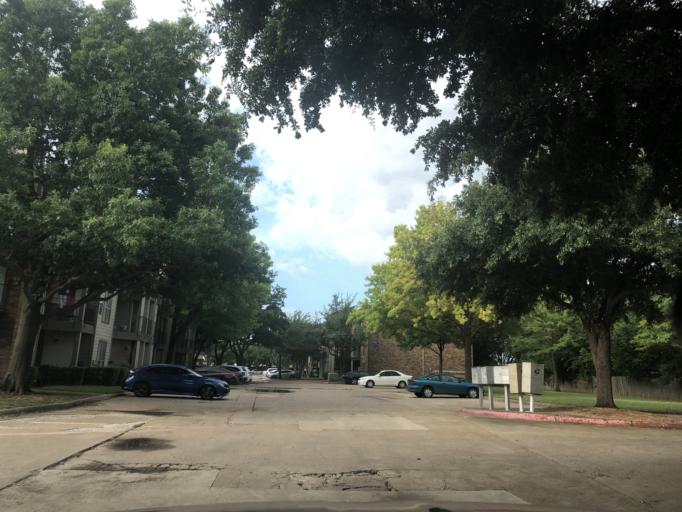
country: US
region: Texas
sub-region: Dallas County
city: Rowlett
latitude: 32.8498
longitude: -96.5773
